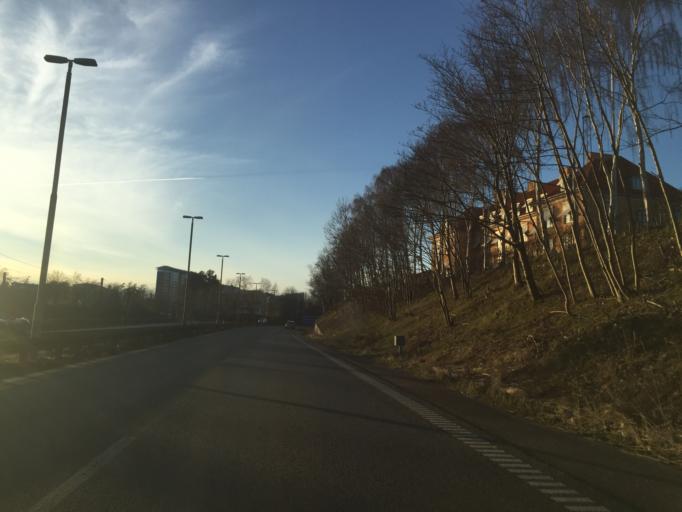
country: DK
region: Capital Region
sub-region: Lyngby-Tarbaek Kommune
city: Kongens Lyngby
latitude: 55.7793
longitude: 12.4885
